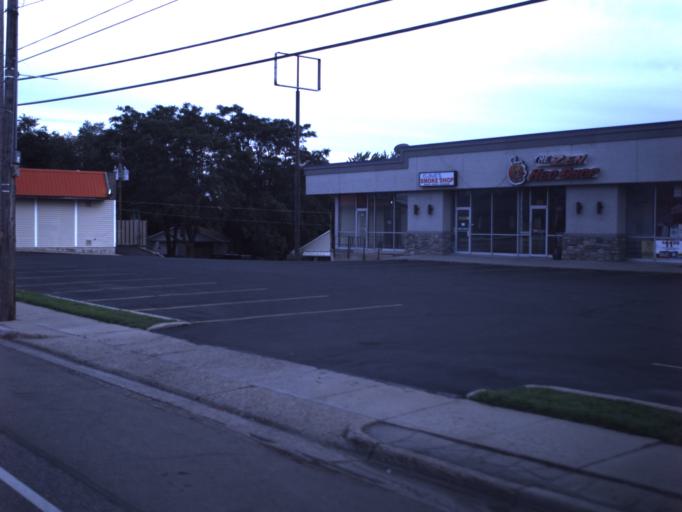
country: US
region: Utah
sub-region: Davis County
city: Clearfield
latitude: 41.1095
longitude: -112.0221
